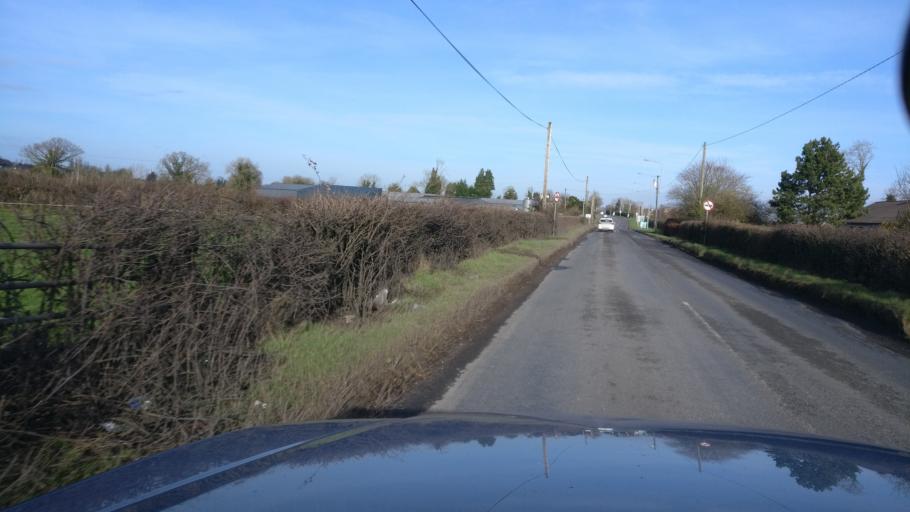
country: IE
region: Leinster
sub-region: Laois
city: Portlaoise
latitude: 53.0237
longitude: -7.2697
